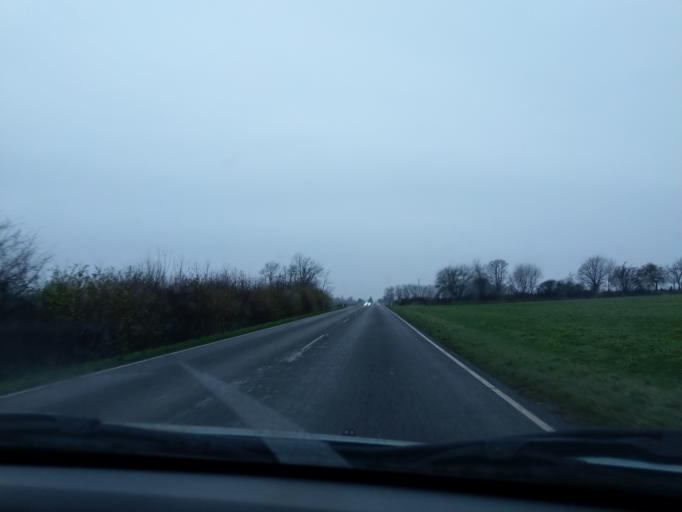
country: DK
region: Zealand
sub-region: Vordingborg Kommune
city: Praesto
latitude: 55.1189
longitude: 11.9825
